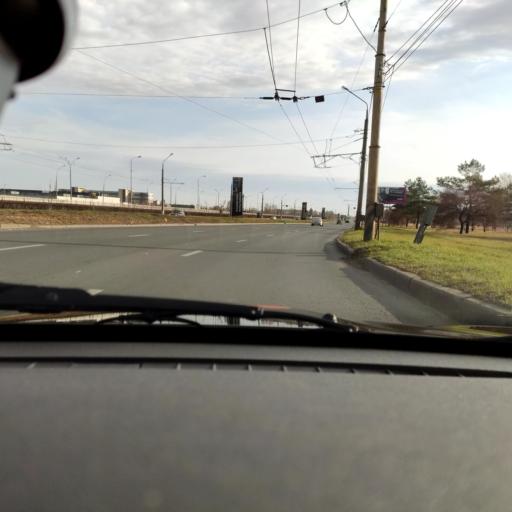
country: RU
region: Samara
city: Tol'yatti
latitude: 53.5546
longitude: 49.2715
